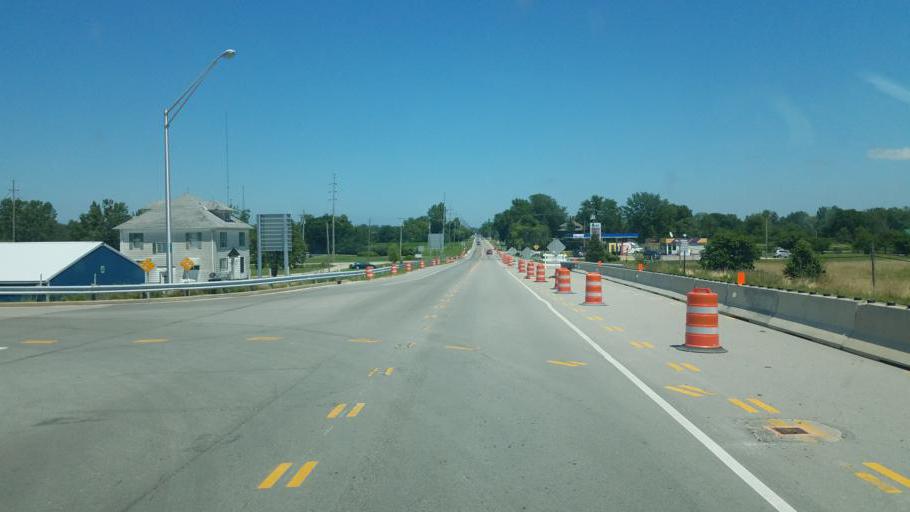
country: US
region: Ohio
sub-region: Ottawa County
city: Port Clinton
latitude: 41.5003
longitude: -82.9691
